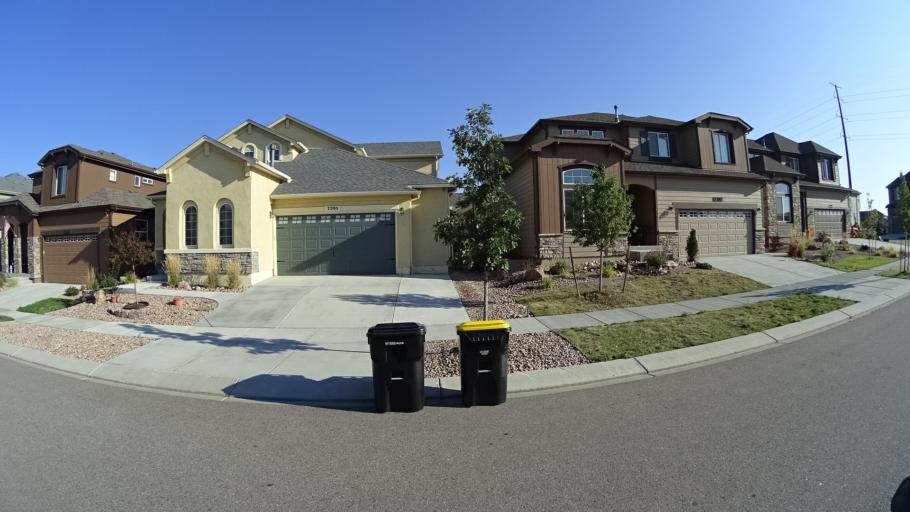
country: US
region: Colorado
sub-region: El Paso County
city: Cimarron Hills
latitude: 38.9345
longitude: -104.6648
